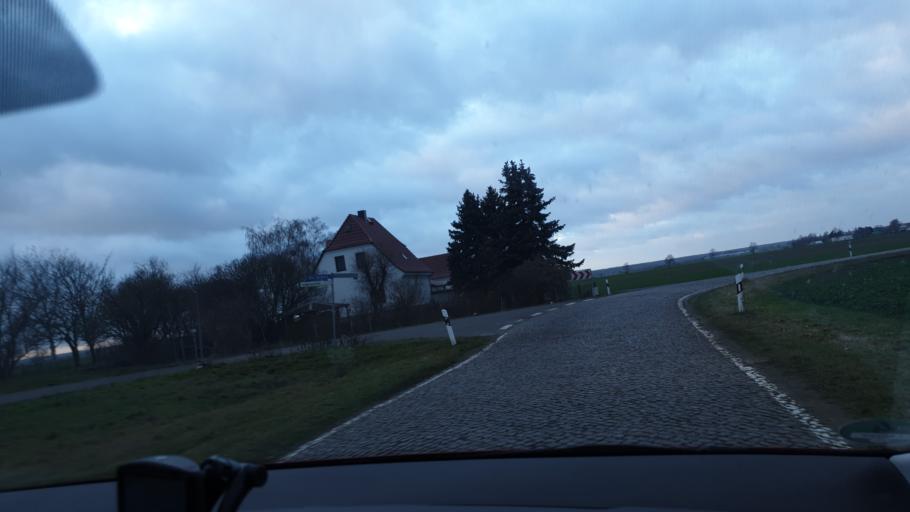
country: DE
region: Saxony
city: Mockrehna
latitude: 51.4702
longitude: 12.8554
